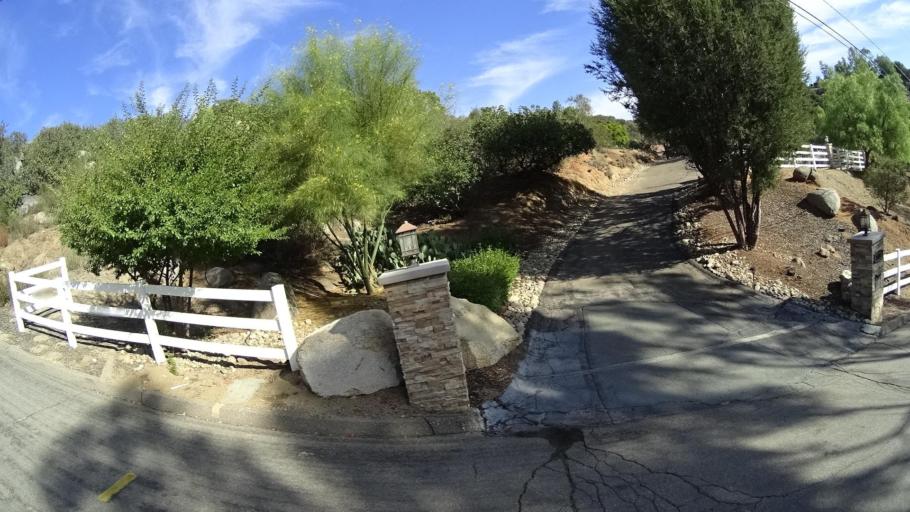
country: US
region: California
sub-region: San Diego County
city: Alpine
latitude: 32.8151
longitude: -116.7501
